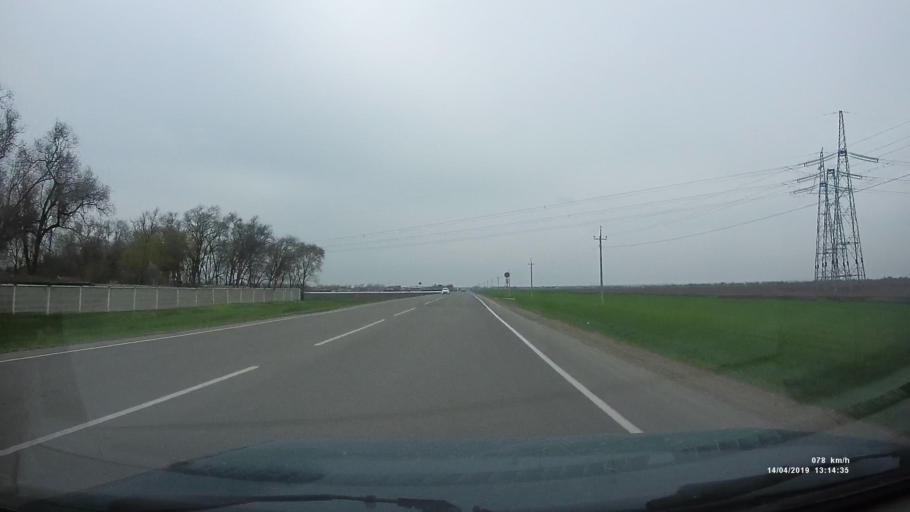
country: RU
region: Rostov
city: Kuleshovka
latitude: 47.0897
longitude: 39.6073
